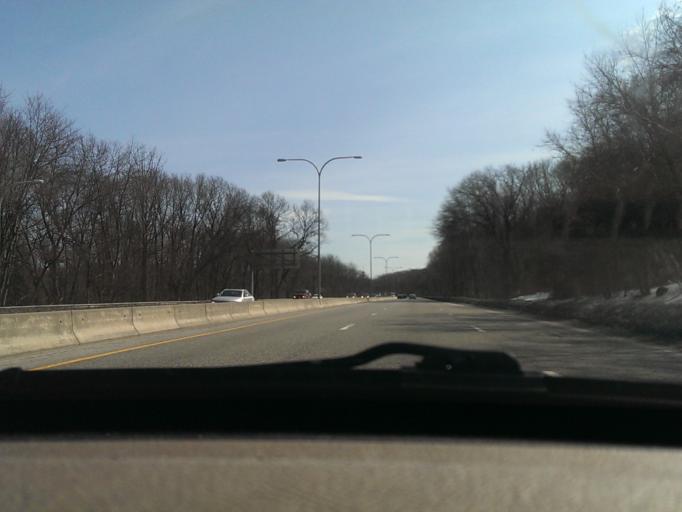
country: US
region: Rhode Island
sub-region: Providence County
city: North Providence
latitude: 41.9010
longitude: -71.4467
